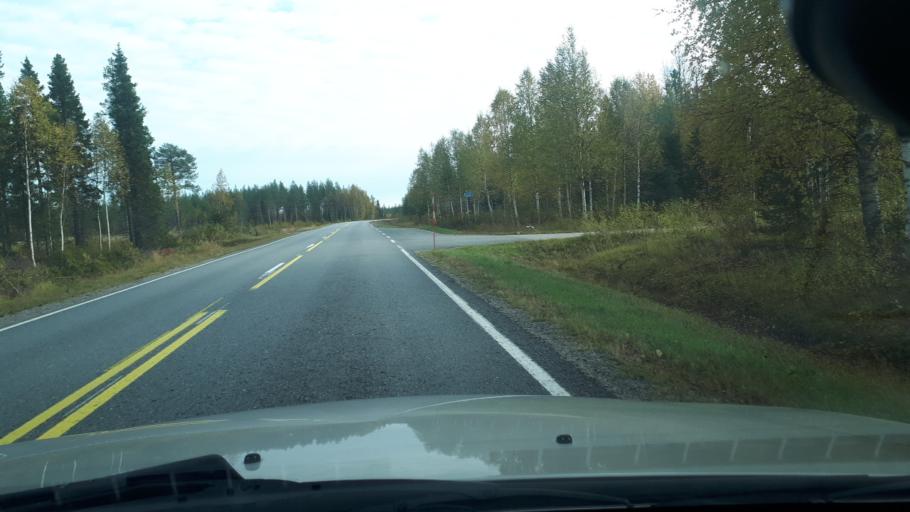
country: FI
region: Lapland
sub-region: Rovaniemi
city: Ranua
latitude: 65.9629
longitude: 25.9592
